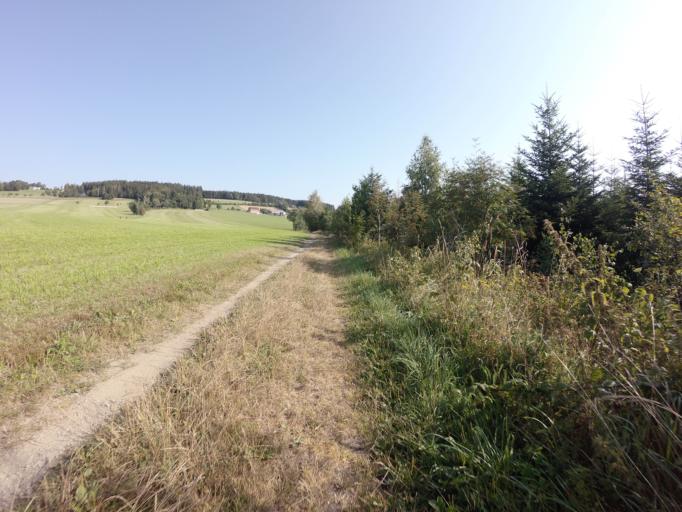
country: AT
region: Upper Austria
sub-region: Politischer Bezirk Urfahr-Umgebung
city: Bad Leonfelden
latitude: 48.5410
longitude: 14.3154
